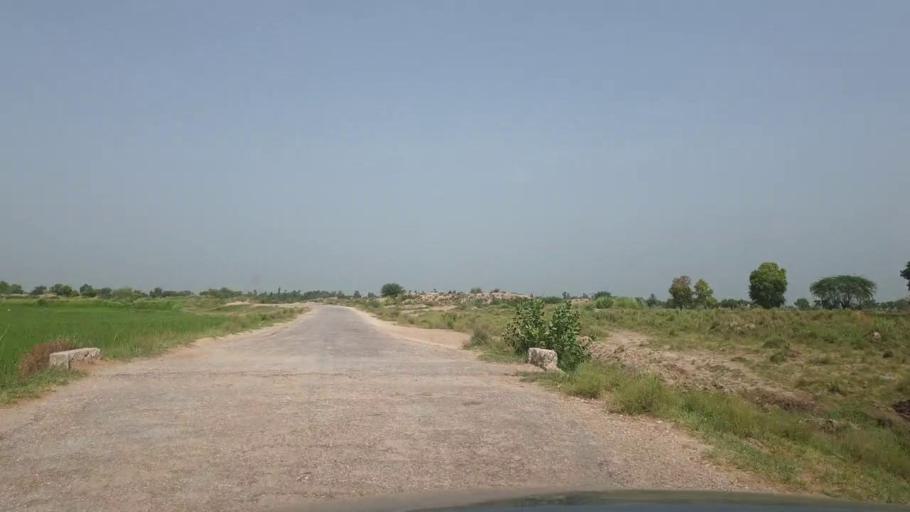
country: PK
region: Sindh
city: Madeji
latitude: 27.8401
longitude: 68.4408
